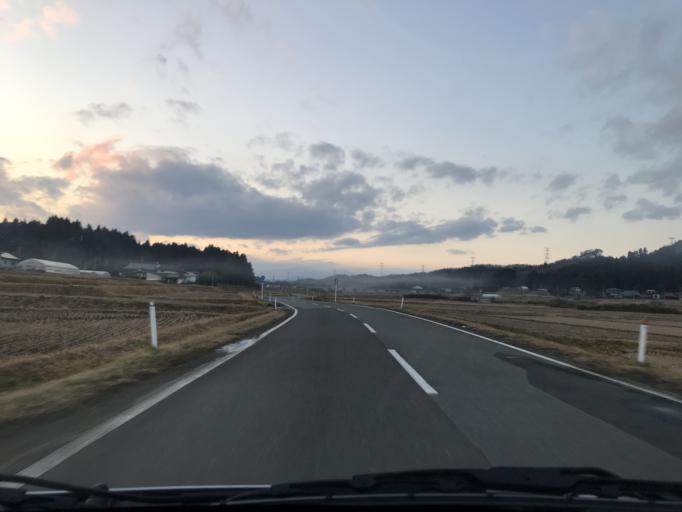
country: JP
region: Iwate
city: Ichinoseki
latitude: 38.8427
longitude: 141.1206
